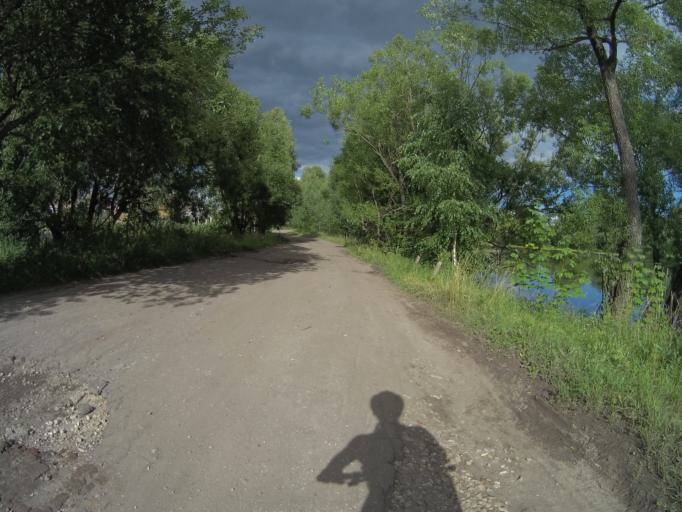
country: RU
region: Vladimir
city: Suzdal'
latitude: 56.3186
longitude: 40.4227
